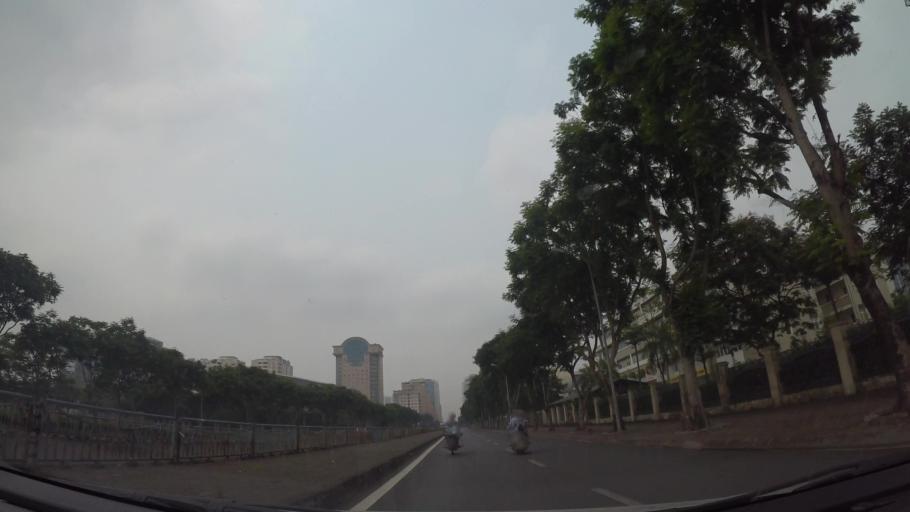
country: VN
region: Ha Noi
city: Cau Dien
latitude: 21.0265
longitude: 105.7633
